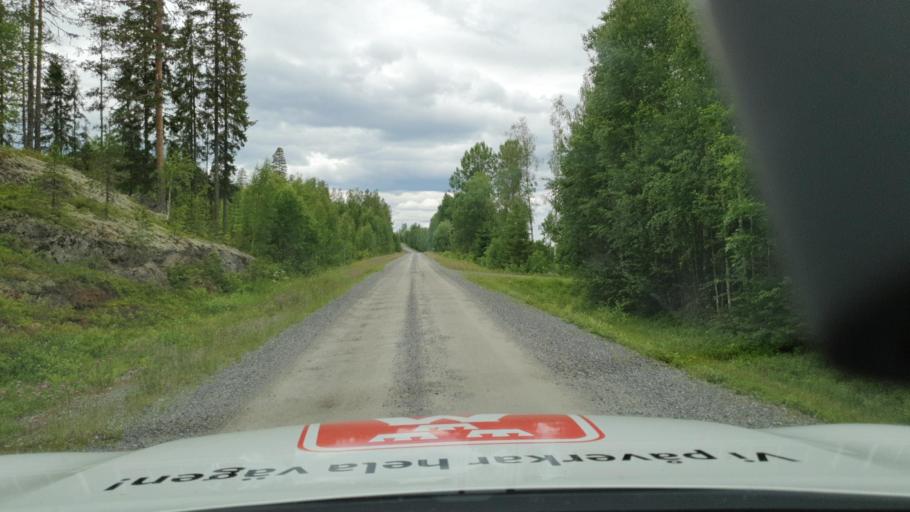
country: SE
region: Vaesterbotten
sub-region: Nordmalings Kommun
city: Nordmaling
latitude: 63.7546
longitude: 19.3715
